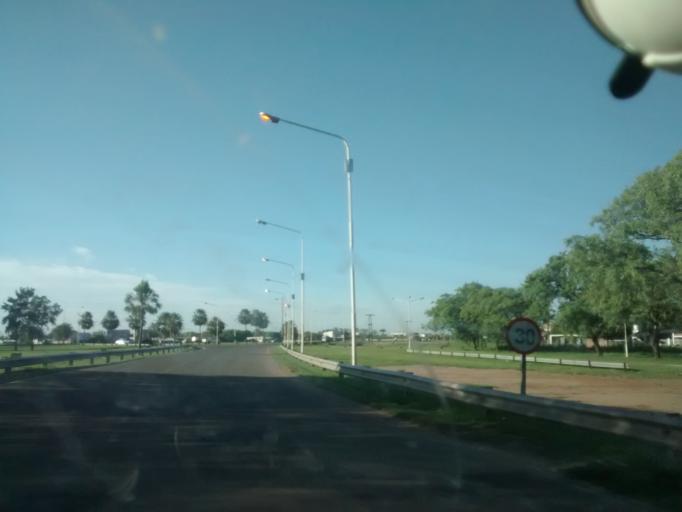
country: AR
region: Chaco
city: Fontana
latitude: -27.4447
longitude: -59.0247
